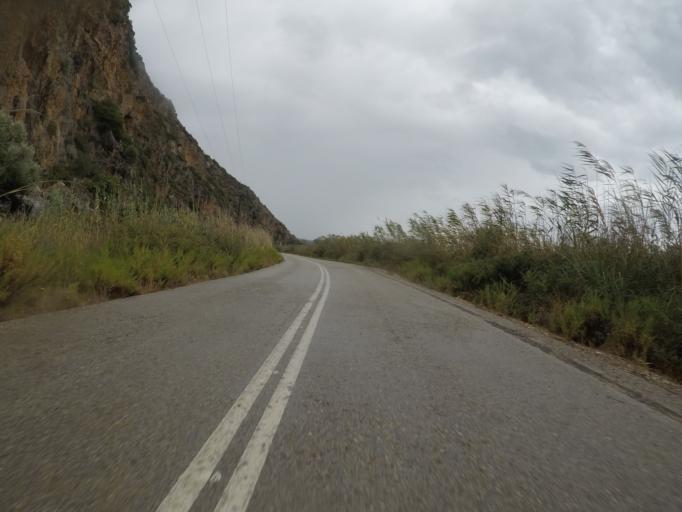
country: GR
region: West Greece
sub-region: Nomos Ileias
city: Zacharo
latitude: 37.5221
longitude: 21.5978
